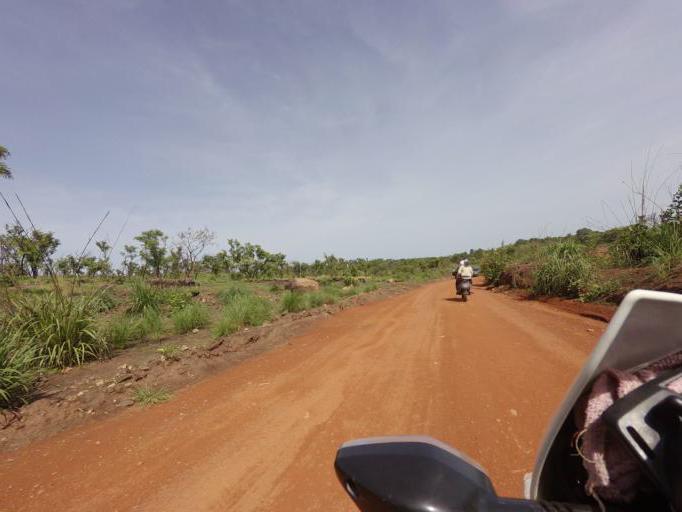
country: SL
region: Northern Province
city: Makeni
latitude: 9.0945
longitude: -12.1967
